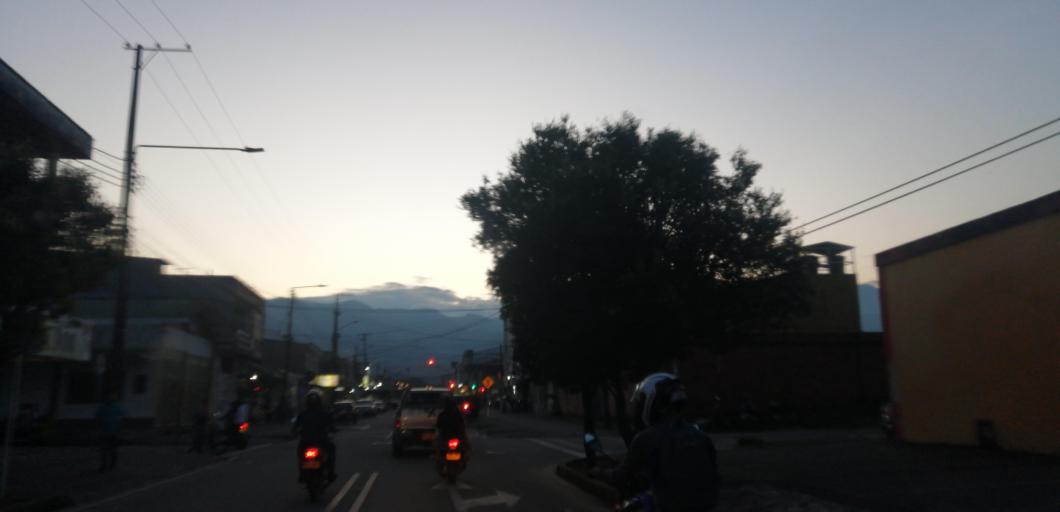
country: CO
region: Meta
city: Acacias
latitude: 3.9879
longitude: -73.7721
